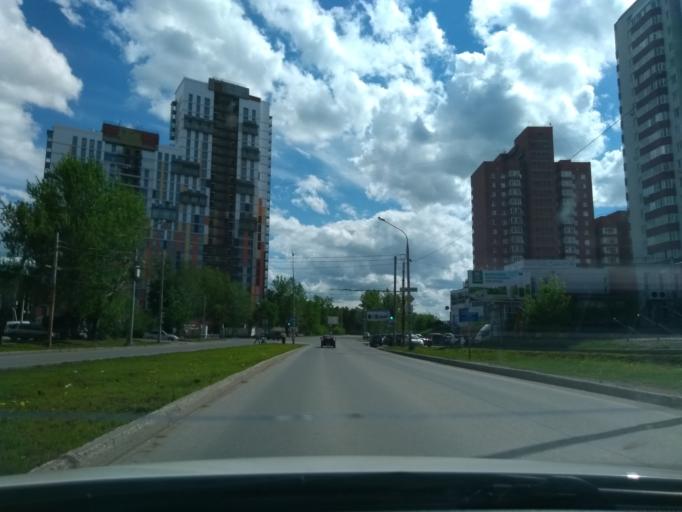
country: RU
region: Perm
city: Kondratovo
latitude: 57.9935
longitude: 56.1365
